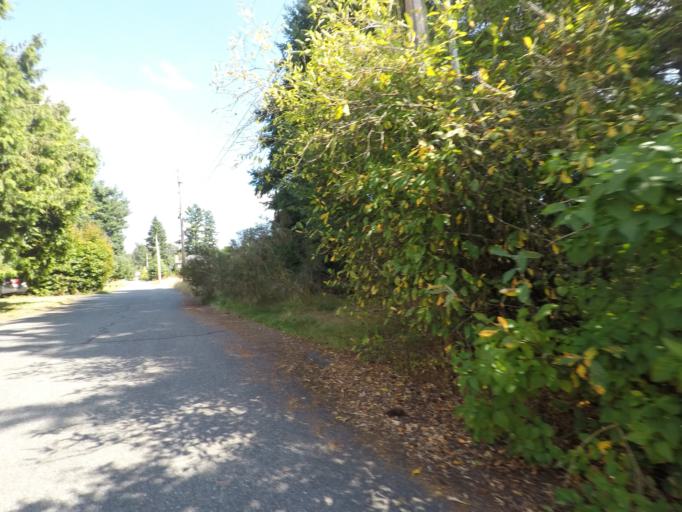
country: US
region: Washington
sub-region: King County
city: Kenmore
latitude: 47.7609
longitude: -122.2365
